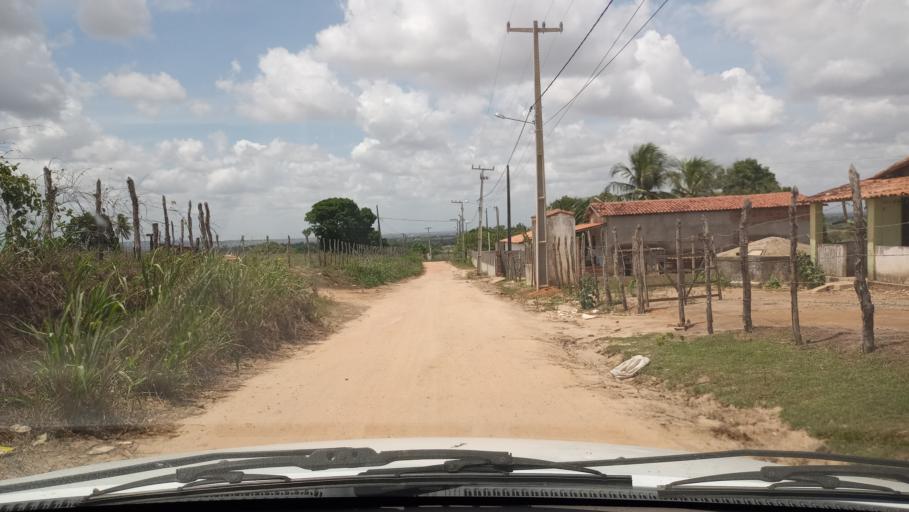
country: BR
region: Rio Grande do Norte
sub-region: Brejinho
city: Brejinho
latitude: -6.2636
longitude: -35.3423
